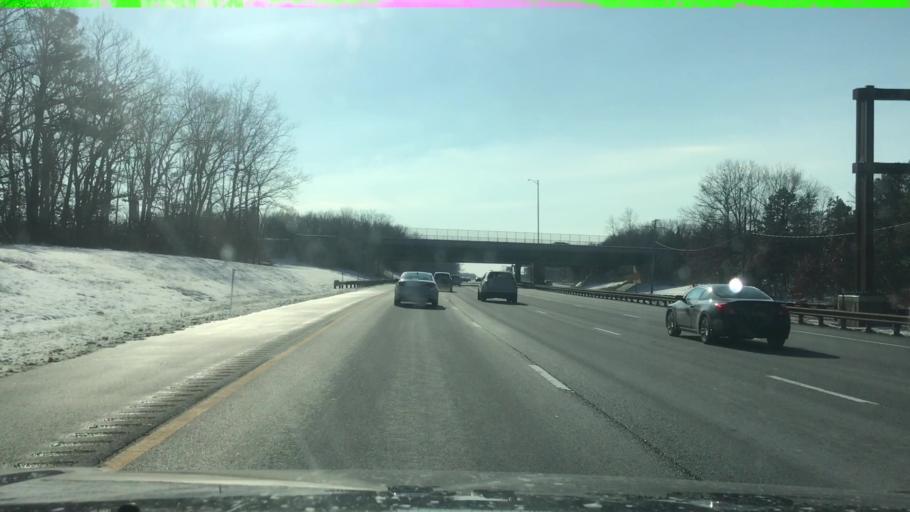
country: US
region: New Jersey
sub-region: Monmouth County
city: Shark River Hills
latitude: 40.1719
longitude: -74.1006
